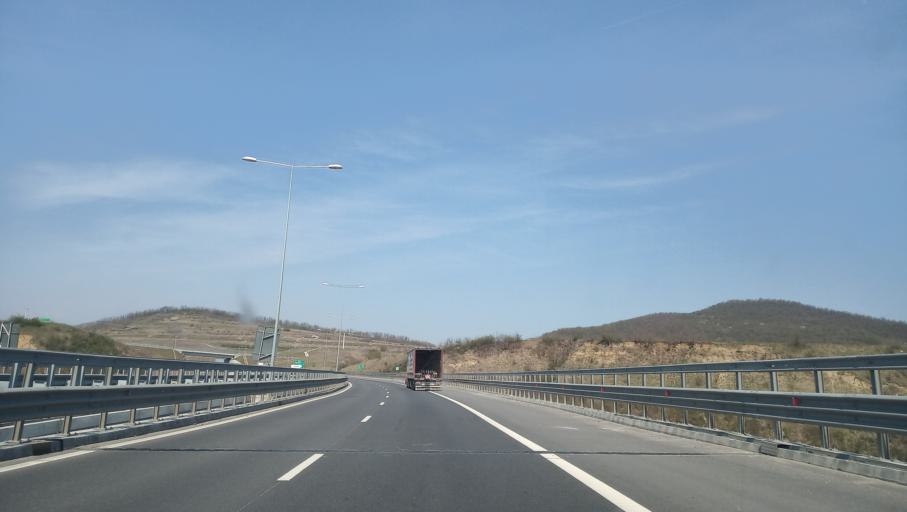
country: RO
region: Alba
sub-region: Municipiul Aiud
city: Aiud
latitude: 46.3389
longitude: 23.7337
